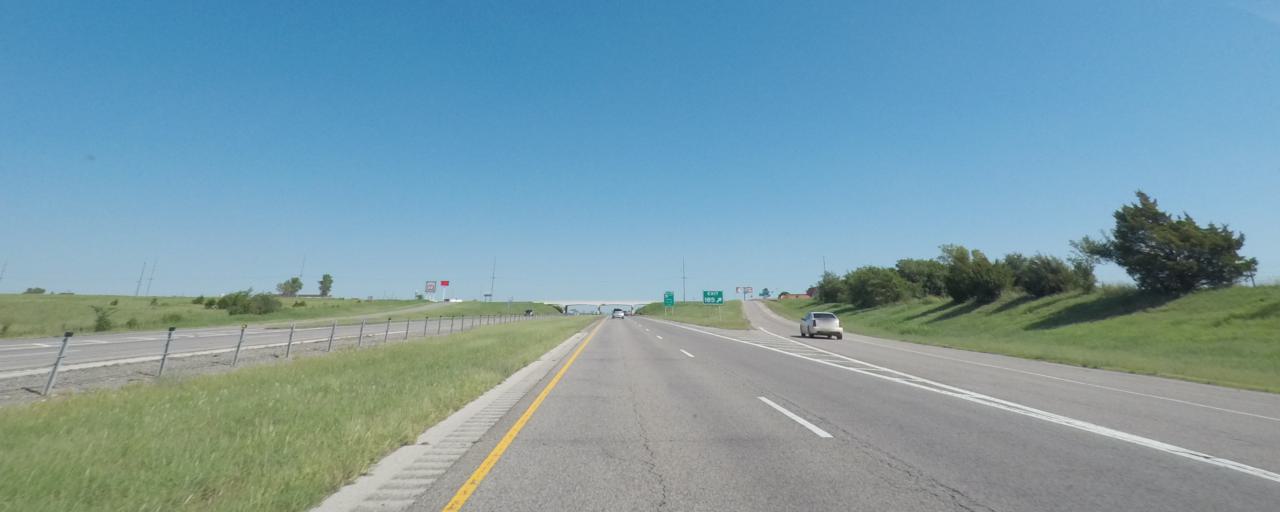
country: US
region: Oklahoma
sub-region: Noble County
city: Perry
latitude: 36.2719
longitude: -97.3276
